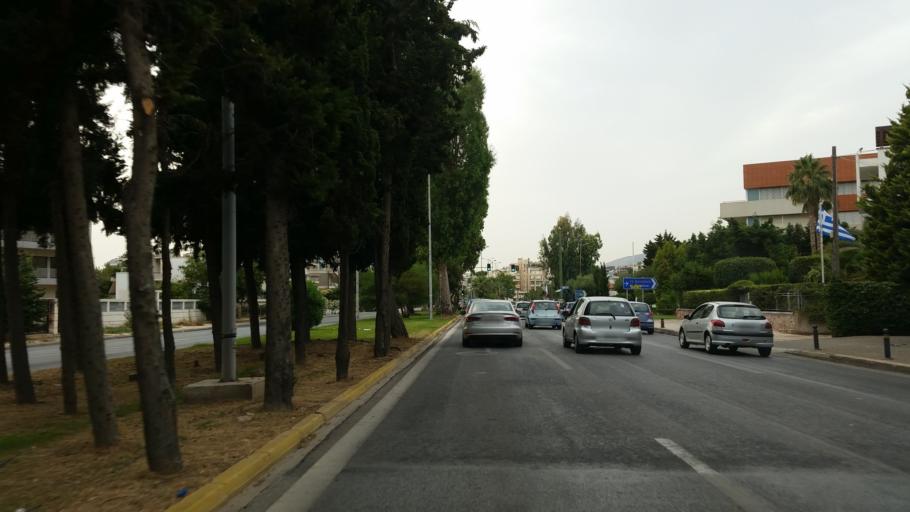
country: GR
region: Attica
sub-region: Nomarchia Anatolikis Attikis
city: Voula
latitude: 37.8323
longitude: 23.7729
